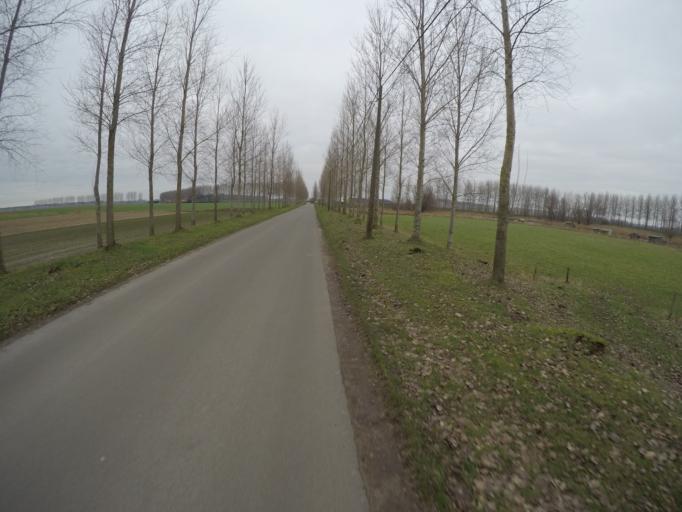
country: BE
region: Flanders
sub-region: Provincie Oost-Vlaanderen
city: Sint-Gillis-Waas
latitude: 51.2426
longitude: 4.1261
